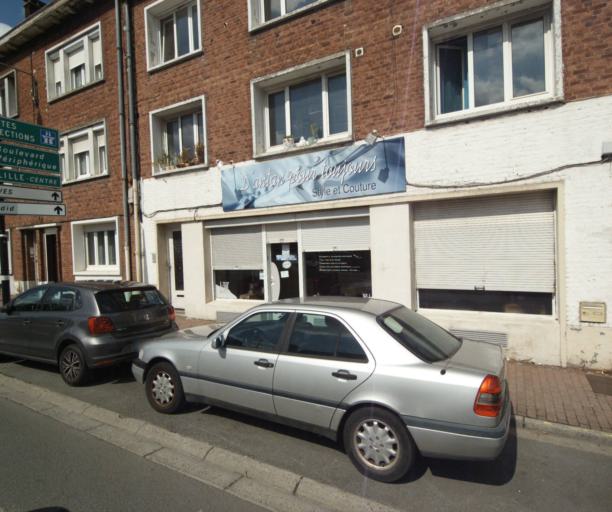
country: FR
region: Nord-Pas-de-Calais
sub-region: Departement du Nord
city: Lezennes
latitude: 50.6222
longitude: 3.0920
